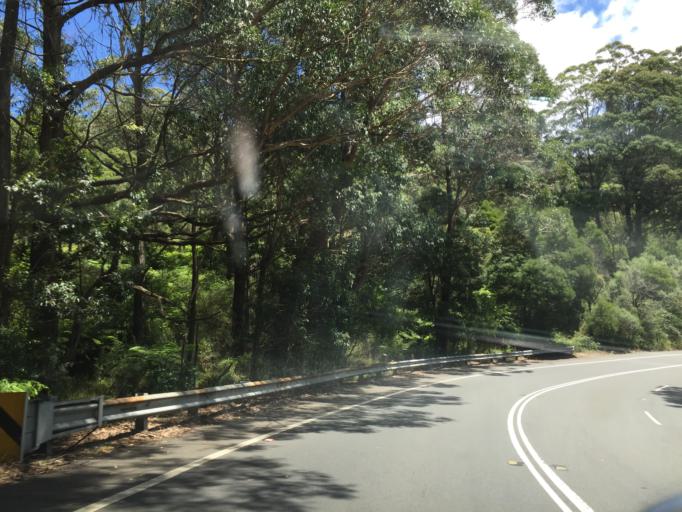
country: AU
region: New South Wales
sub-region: Blue Mountains Municipality
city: Blackheath
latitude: -33.5498
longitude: 150.4182
